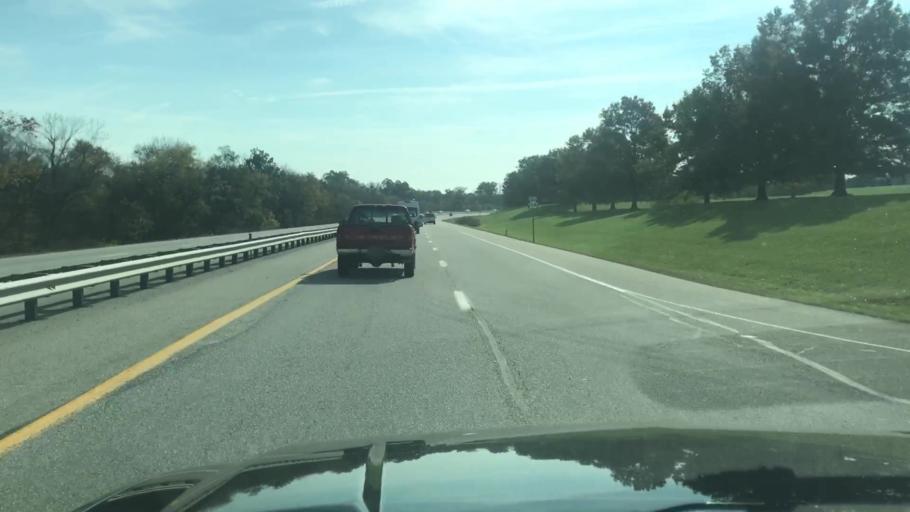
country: US
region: Pennsylvania
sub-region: Cumberland County
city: Mechanicsburg
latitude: 40.2587
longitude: -77.0359
